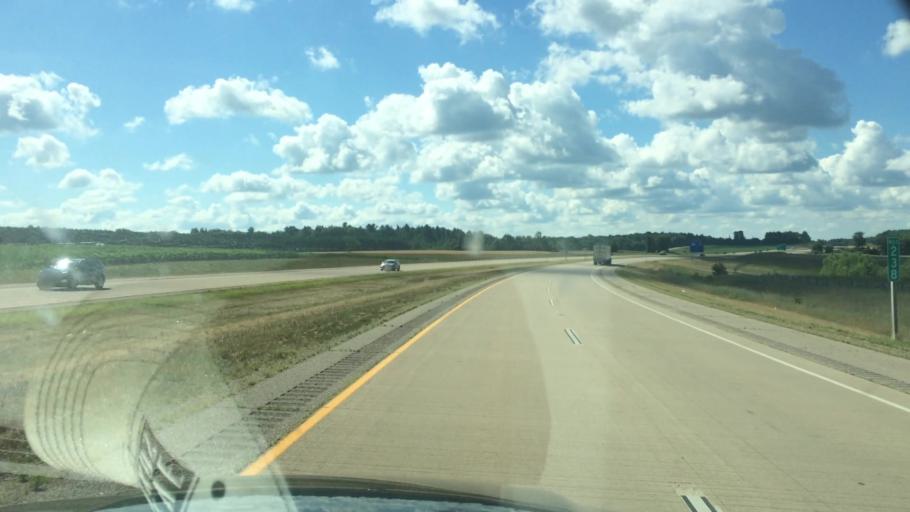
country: US
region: Wisconsin
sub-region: Portage County
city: Amherst
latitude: 44.4627
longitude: -89.3140
